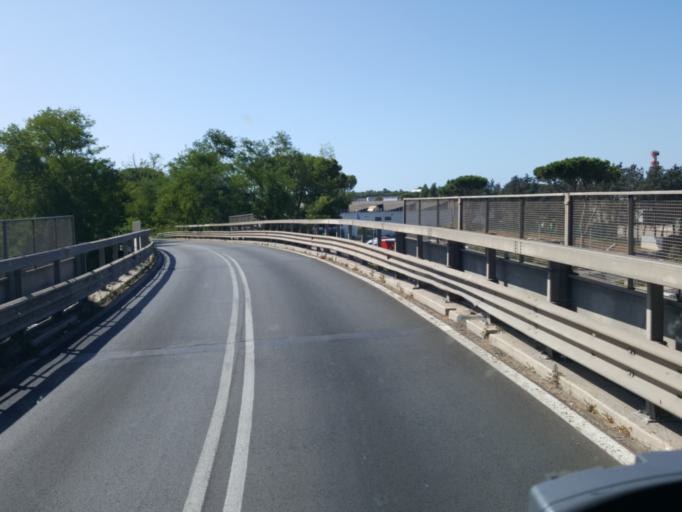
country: IT
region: Latium
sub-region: Citta metropolitana di Roma Capitale
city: Anzio
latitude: 41.5150
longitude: 12.6301
